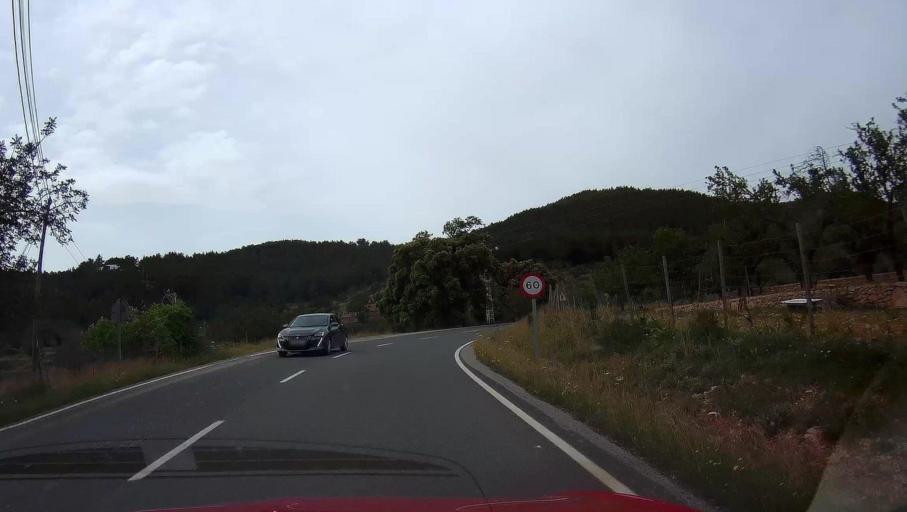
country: ES
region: Balearic Islands
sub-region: Illes Balears
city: Sant Joan de Labritja
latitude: 39.0844
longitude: 1.4991
